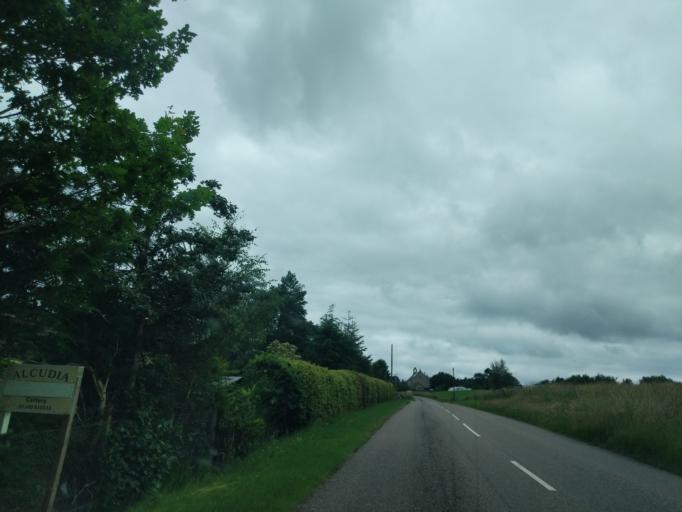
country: GB
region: Scotland
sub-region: Moray
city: Rothes
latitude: 57.4841
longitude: -3.2559
